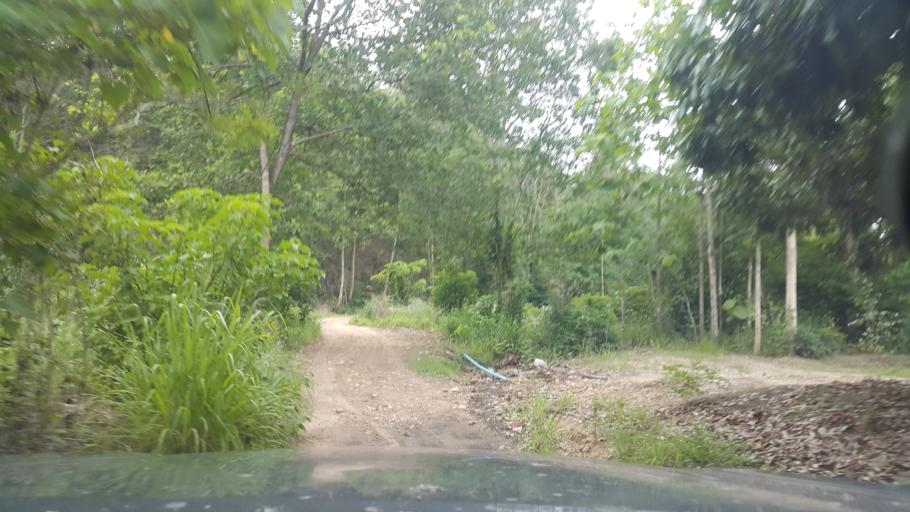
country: TH
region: Chiang Mai
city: San Pa Tong
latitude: 18.6811
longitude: 98.8418
